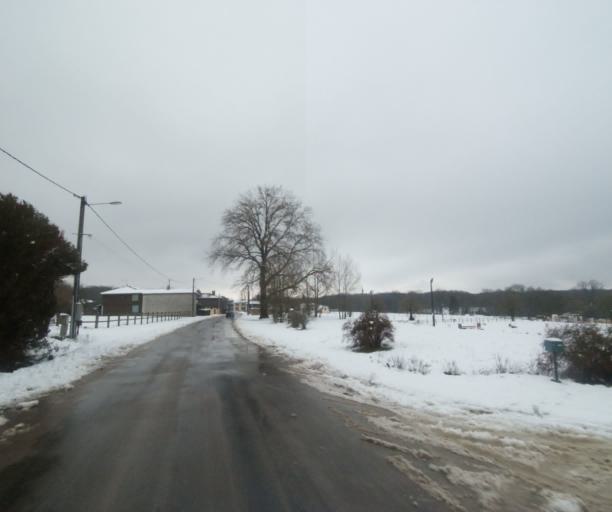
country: FR
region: Champagne-Ardenne
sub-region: Departement de la Haute-Marne
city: Laneuville-a-Remy
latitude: 48.4764
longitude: 4.8840
